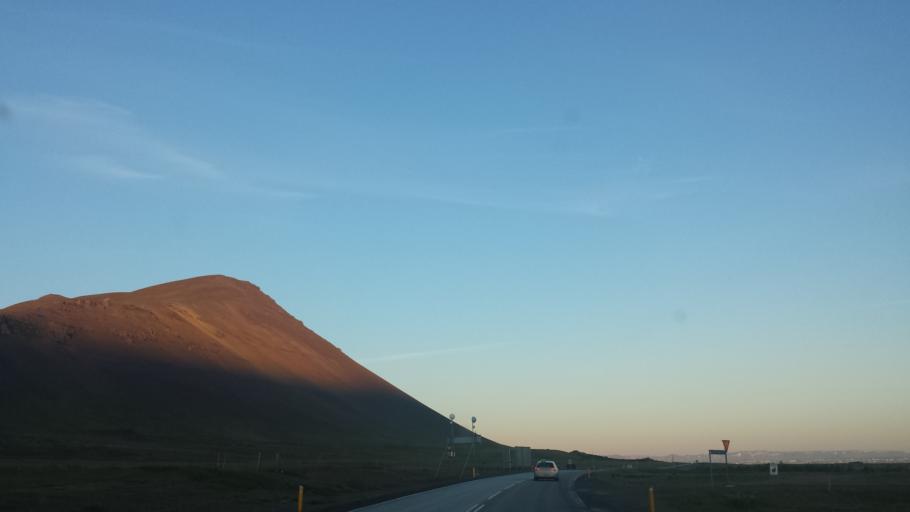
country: IS
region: Capital Region
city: Reykjavik
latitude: 64.2721
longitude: -21.8361
